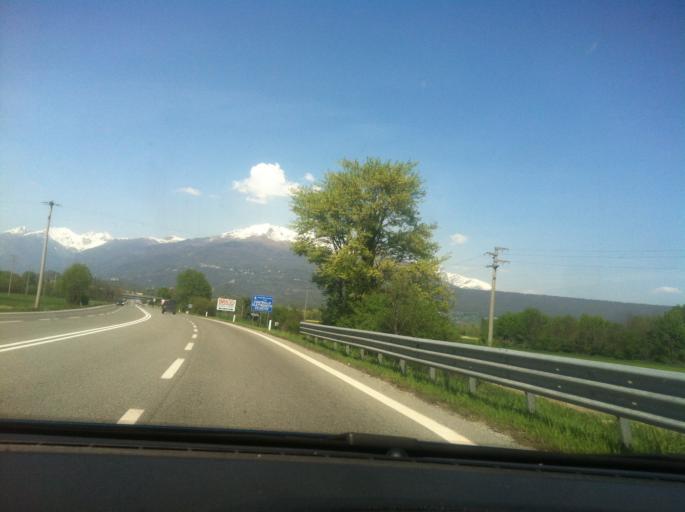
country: IT
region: Piedmont
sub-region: Provincia di Torino
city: Ivrea
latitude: 45.4484
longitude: 7.8888
